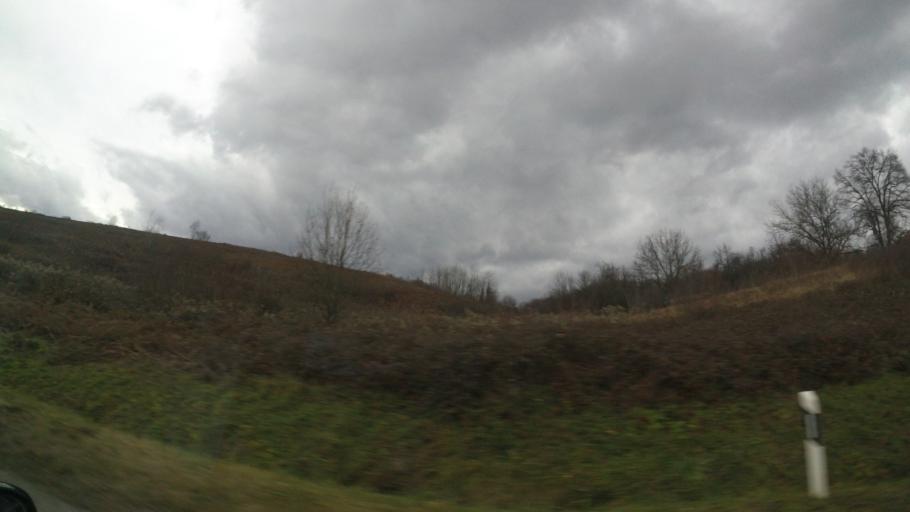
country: HR
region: Karlovacka
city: Vojnic
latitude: 45.3294
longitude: 15.6460
